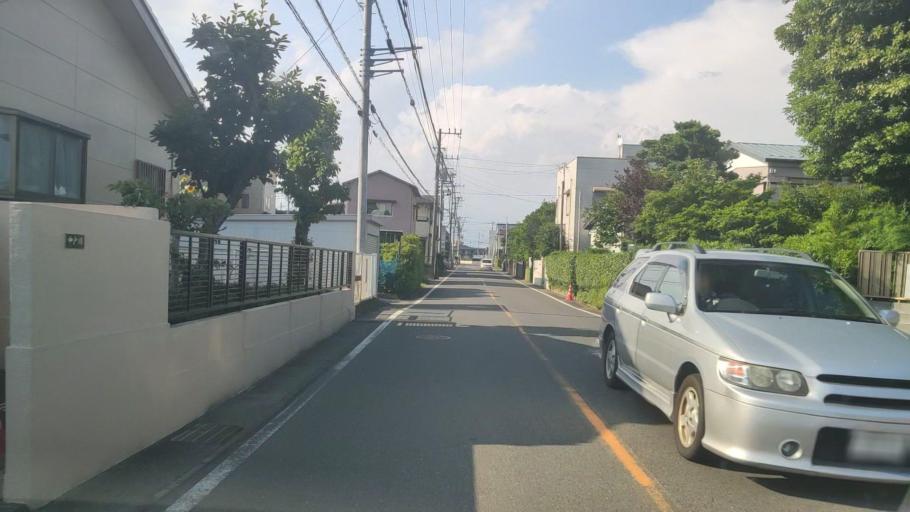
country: JP
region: Kanagawa
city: Hiratsuka
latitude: 35.3575
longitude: 139.3272
